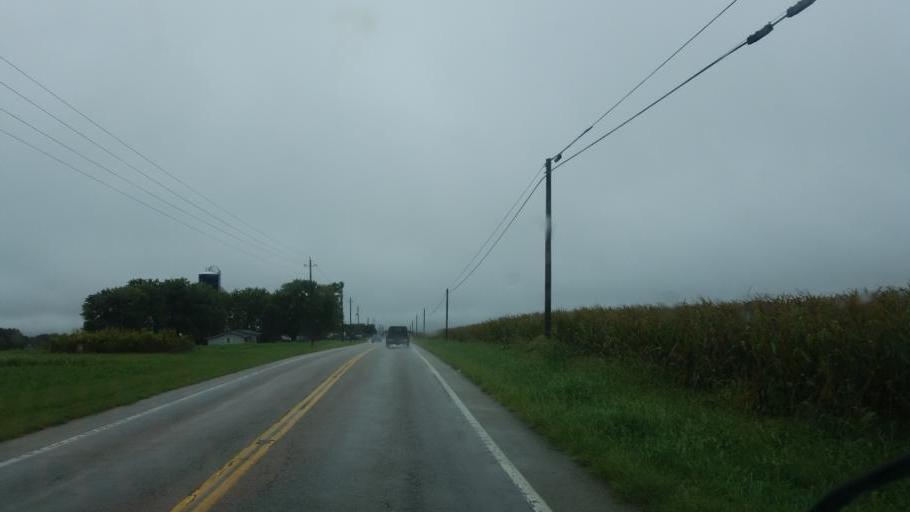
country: US
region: Ohio
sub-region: Adams County
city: West Union
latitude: 38.7974
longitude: -83.4916
